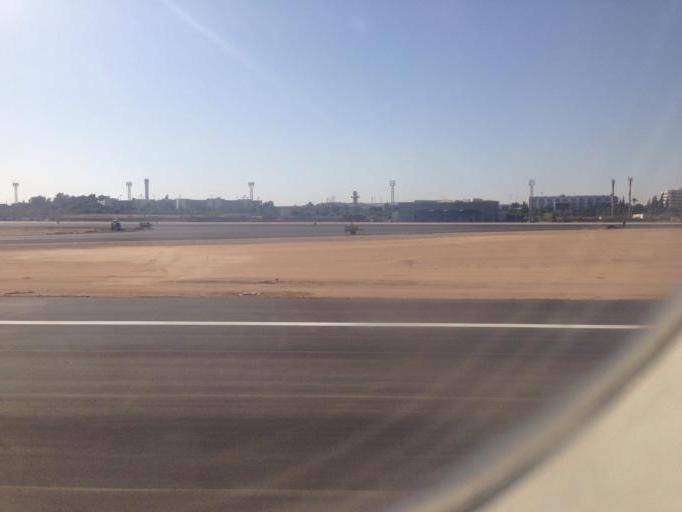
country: EG
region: Muhafazat al Qalyubiyah
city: Al Khankah
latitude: 30.1250
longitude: 31.3872
